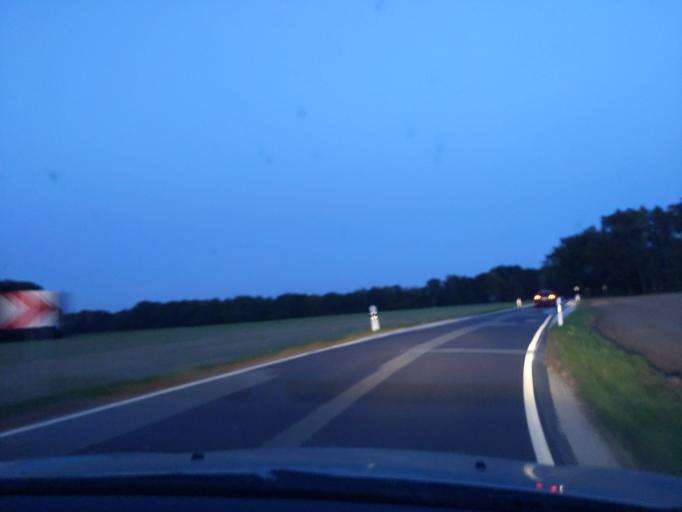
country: DE
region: Saxony
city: Grossdubrau
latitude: 51.2884
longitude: 14.4749
